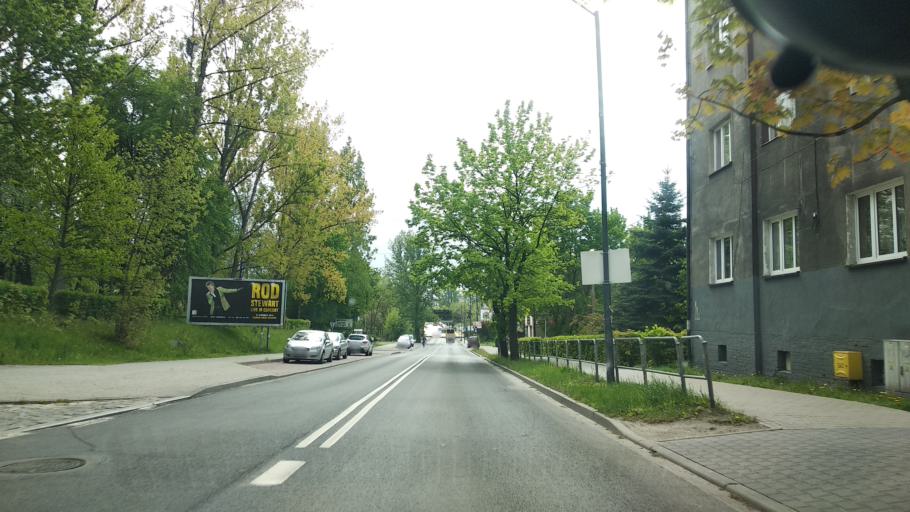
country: PL
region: Silesian Voivodeship
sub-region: Katowice
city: Katowice
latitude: 50.2400
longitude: 18.9806
